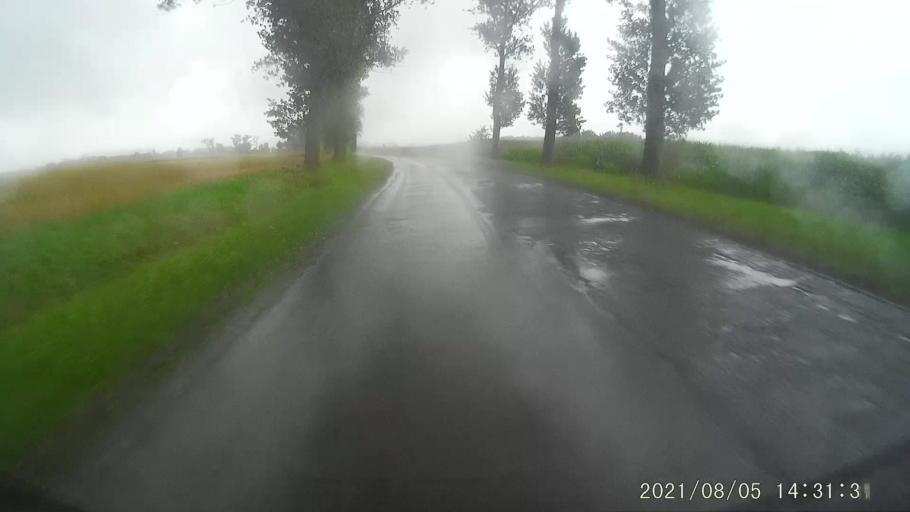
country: PL
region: Opole Voivodeship
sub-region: Powiat nyski
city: Korfantow
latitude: 50.4739
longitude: 17.5562
